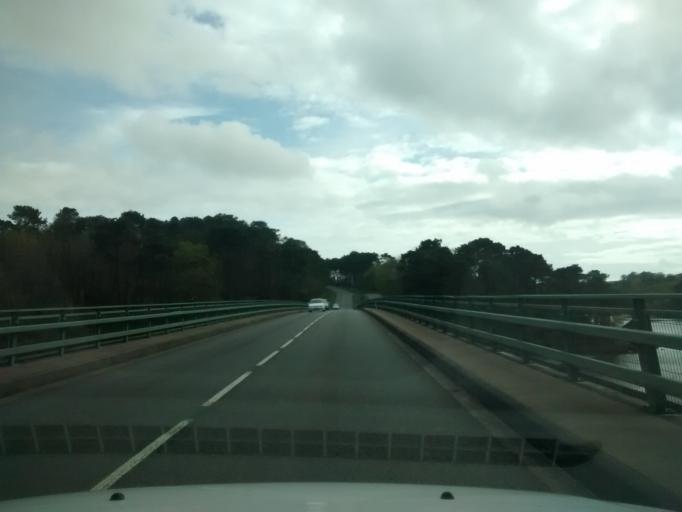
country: FR
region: Brittany
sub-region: Departement du Morbihan
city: Guidel-Plage
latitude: 47.7978
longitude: -3.5233
